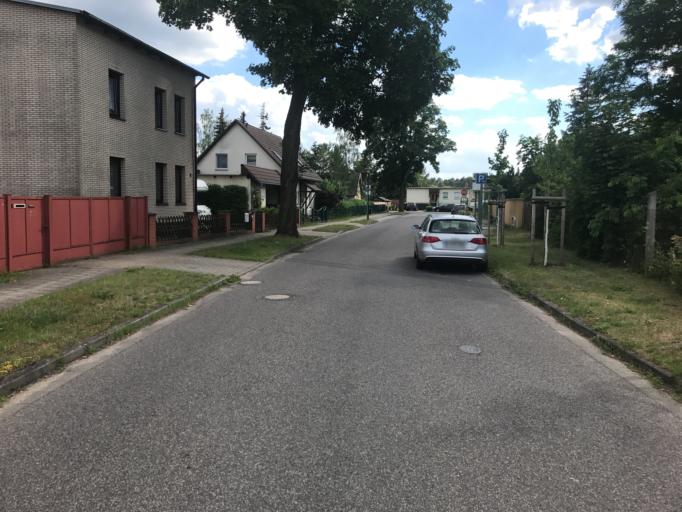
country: DE
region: Brandenburg
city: Marienwerder
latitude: 52.8521
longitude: 13.6720
